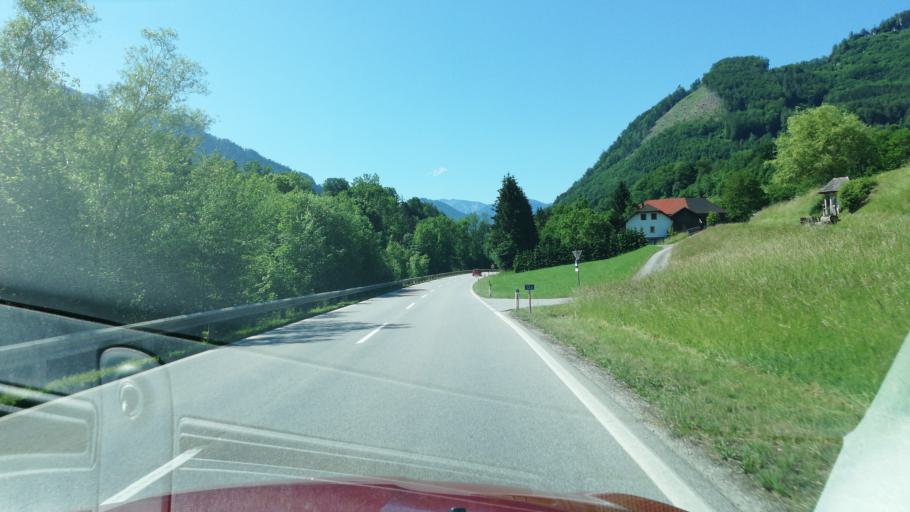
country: AT
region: Upper Austria
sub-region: Politischer Bezirk Kirchdorf an der Krems
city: Gruenburg
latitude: 47.9381
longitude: 14.2485
